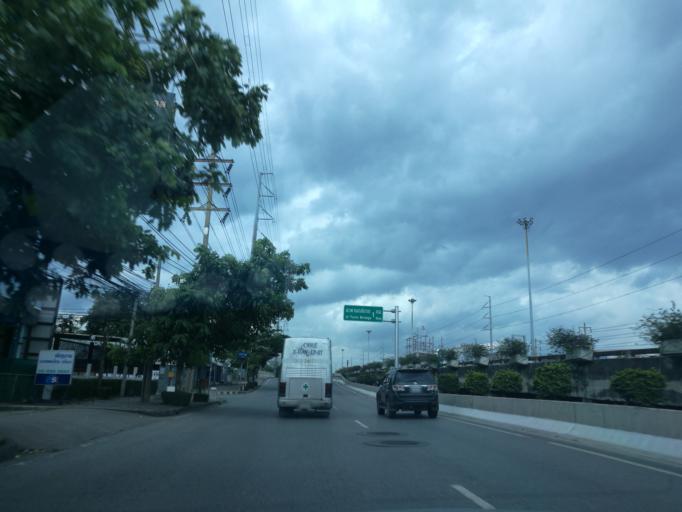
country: TH
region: Bangkok
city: Bang Khun Thian
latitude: 13.6666
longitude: 100.4458
